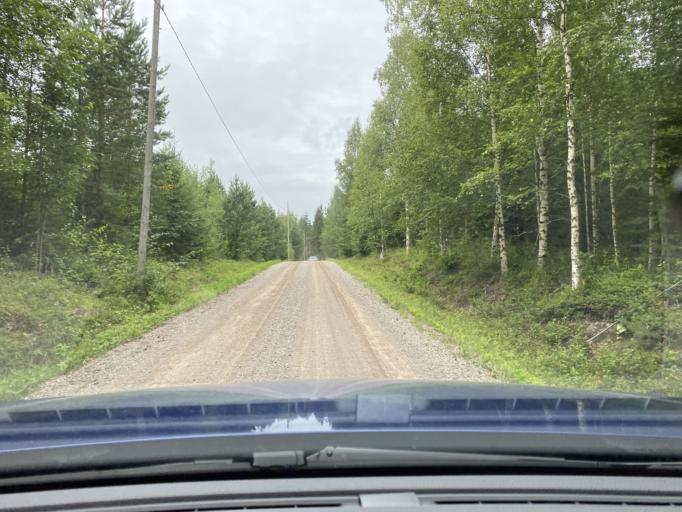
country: FI
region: Pirkanmaa
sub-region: Ylae-Pirkanmaa
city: Maenttae
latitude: 62.0216
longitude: 24.7305
